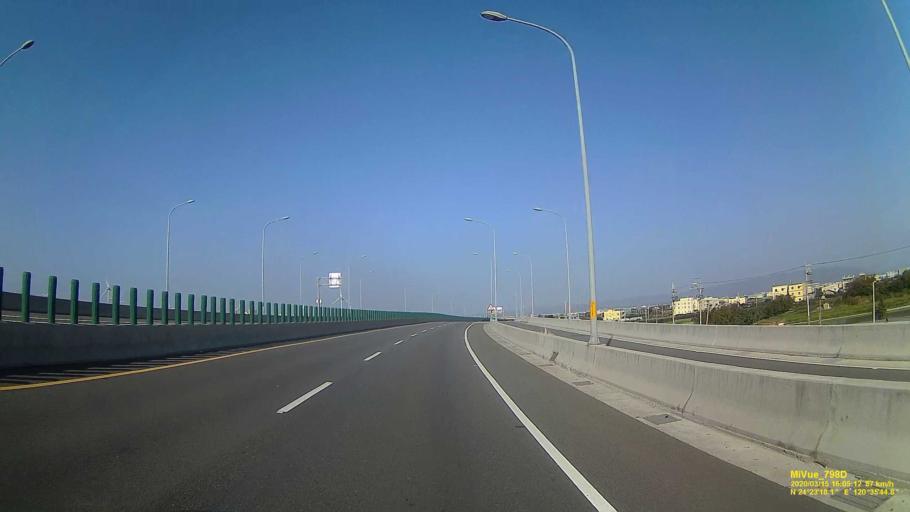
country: TW
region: Taiwan
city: Fengyuan
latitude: 24.3890
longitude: 120.5960
